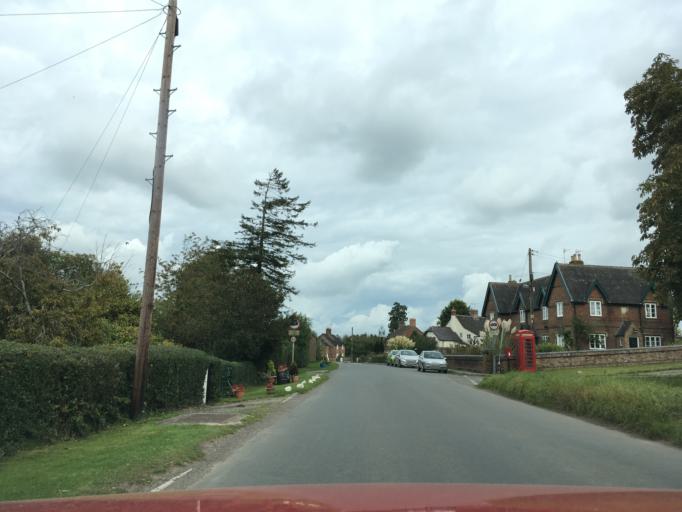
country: GB
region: England
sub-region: Gloucestershire
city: Berkeley
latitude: 51.6826
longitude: -2.4651
